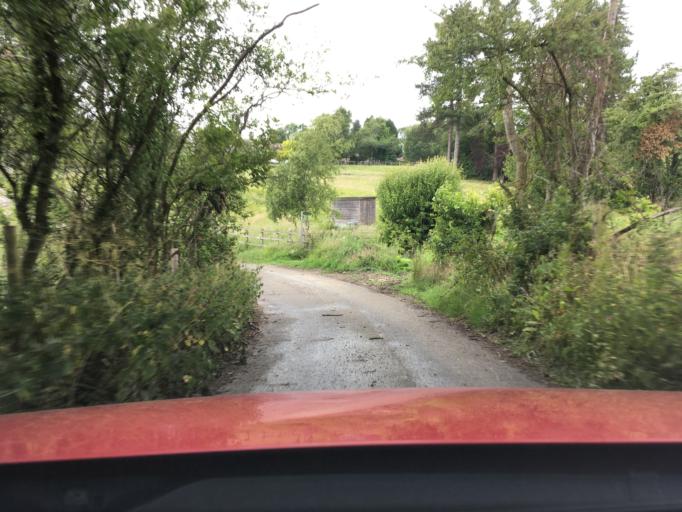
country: GB
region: England
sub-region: Gloucestershire
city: Winchcombe
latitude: 51.9512
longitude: -1.9935
